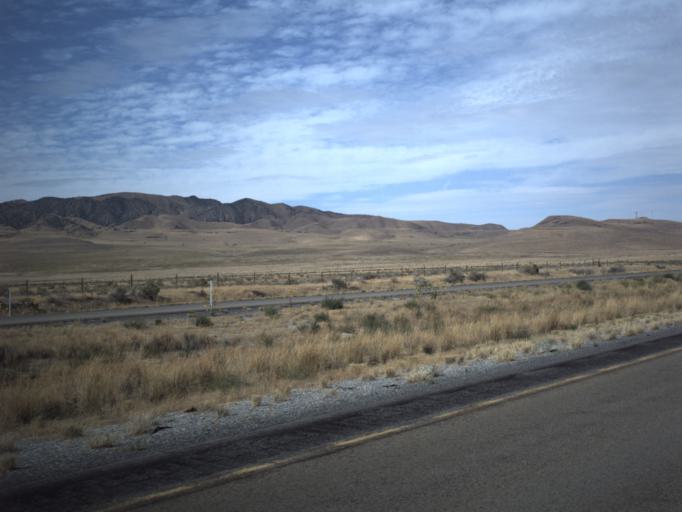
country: US
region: Utah
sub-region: Tooele County
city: Grantsville
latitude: 40.7843
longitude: -112.8204
